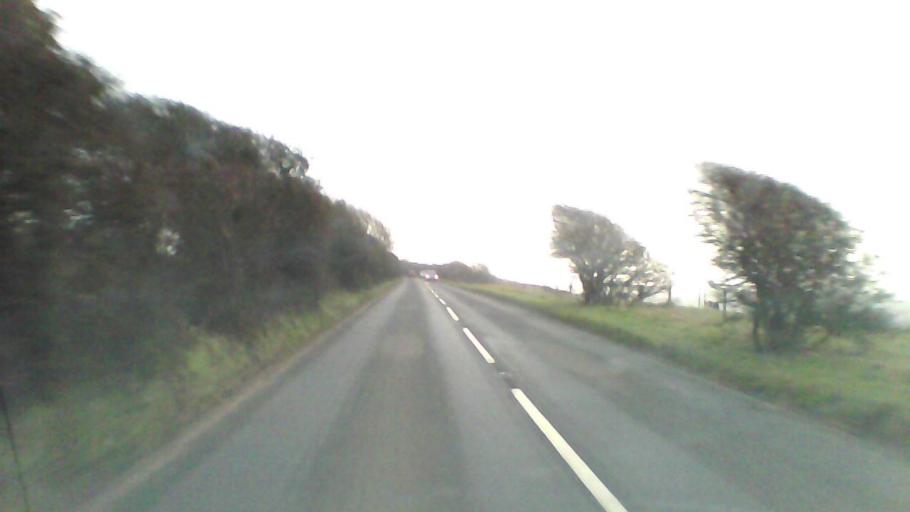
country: GB
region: England
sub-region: Isle of Wight
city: Newchurch
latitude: 50.6827
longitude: -1.2369
